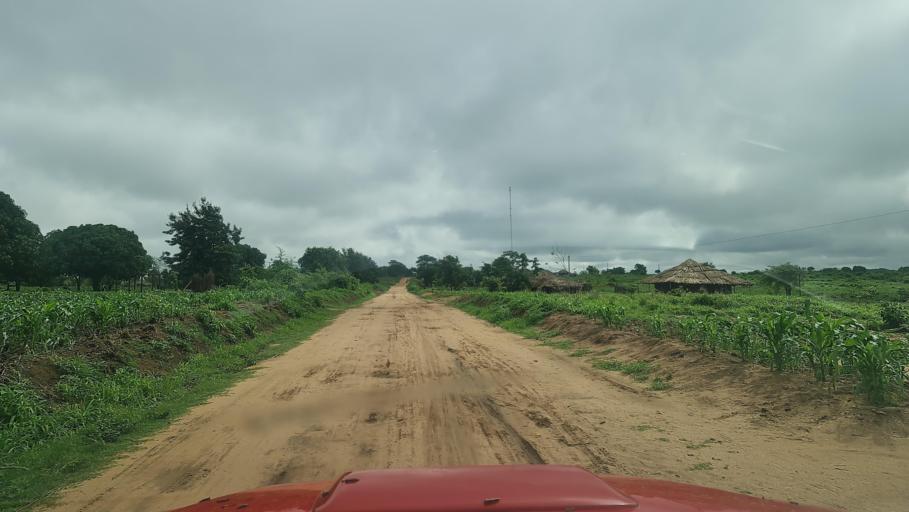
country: MW
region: Southern Region
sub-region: Nsanje District
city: Nsanje
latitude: -17.1923
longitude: 35.7036
